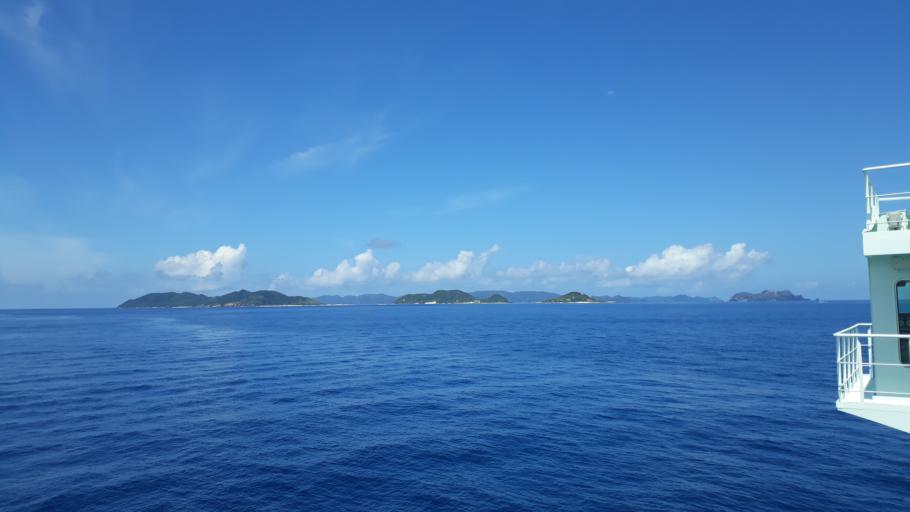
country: JP
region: Okinawa
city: Naha-shi
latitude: 26.2458
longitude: 127.4981
